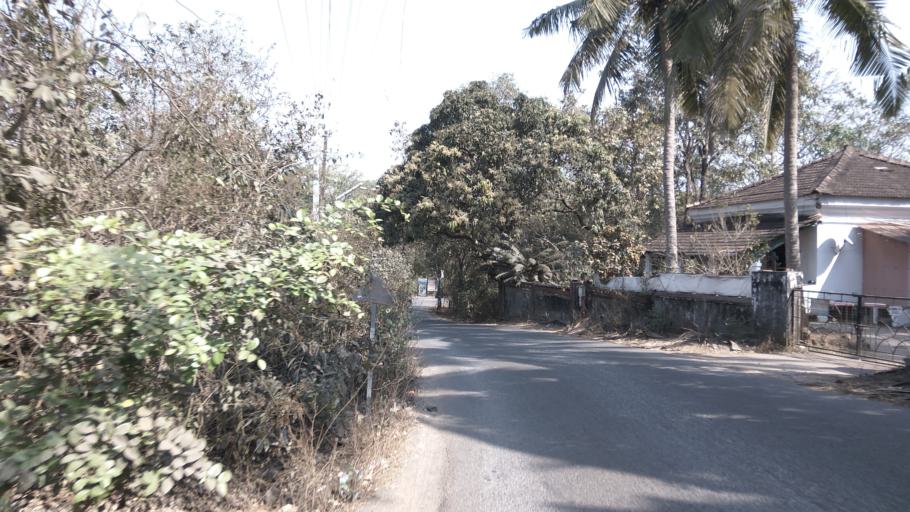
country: IN
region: Goa
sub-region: North Goa
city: Vagator
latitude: 15.5870
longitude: 73.7602
